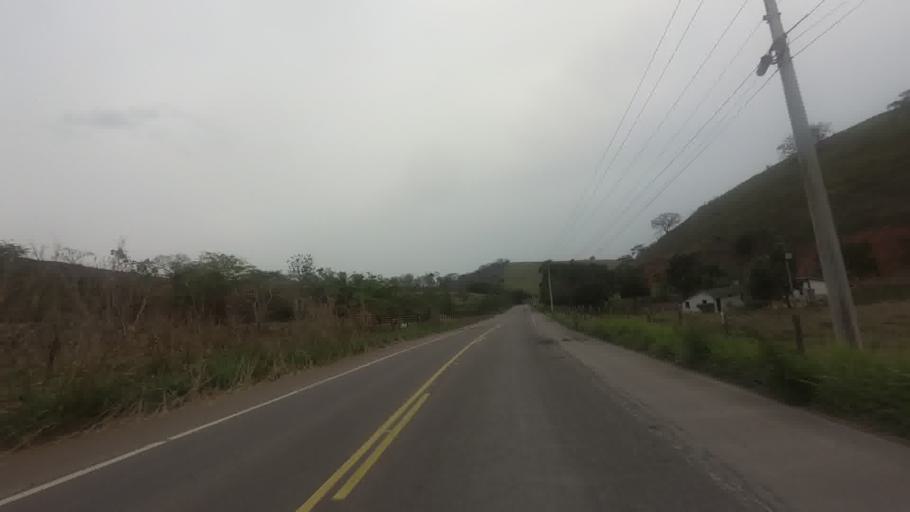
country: BR
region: Rio de Janeiro
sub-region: Santo Antonio De Padua
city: Santo Antonio de Padua
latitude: -21.5751
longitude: -42.2096
